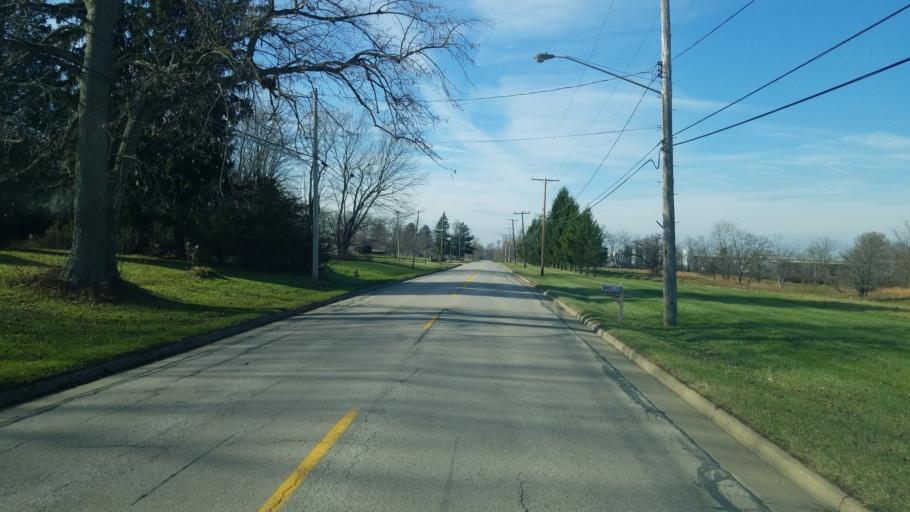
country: US
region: Ohio
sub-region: Ashtabula County
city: Jefferson
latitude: 41.7383
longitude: -80.7854
